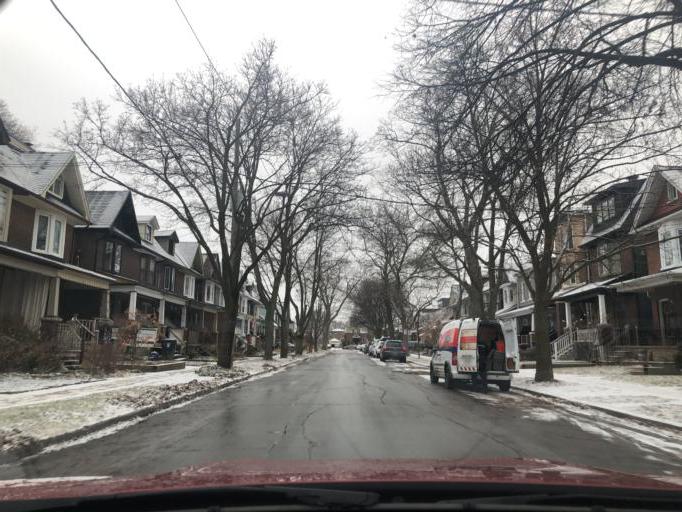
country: CA
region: Ontario
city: Toronto
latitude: 43.6827
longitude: -79.3418
